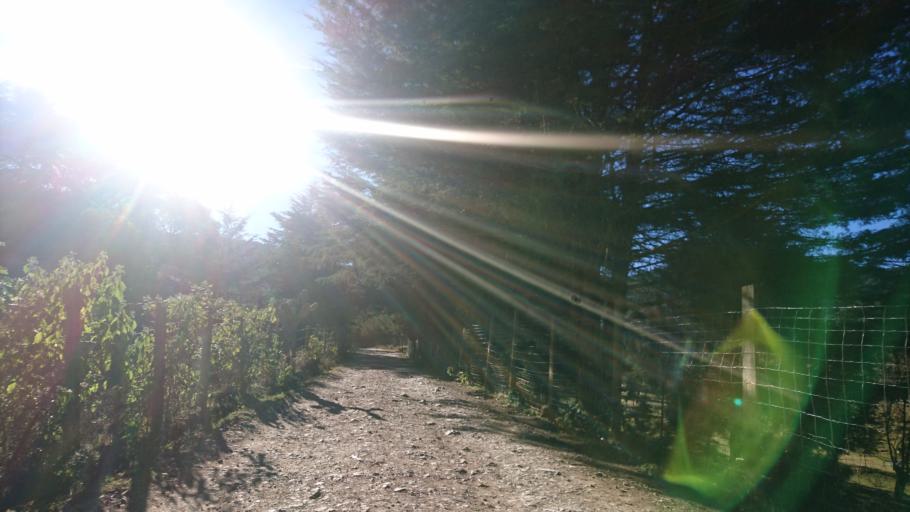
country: MX
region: San Luis Potosi
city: Zaragoza
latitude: 22.0311
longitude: -100.6105
